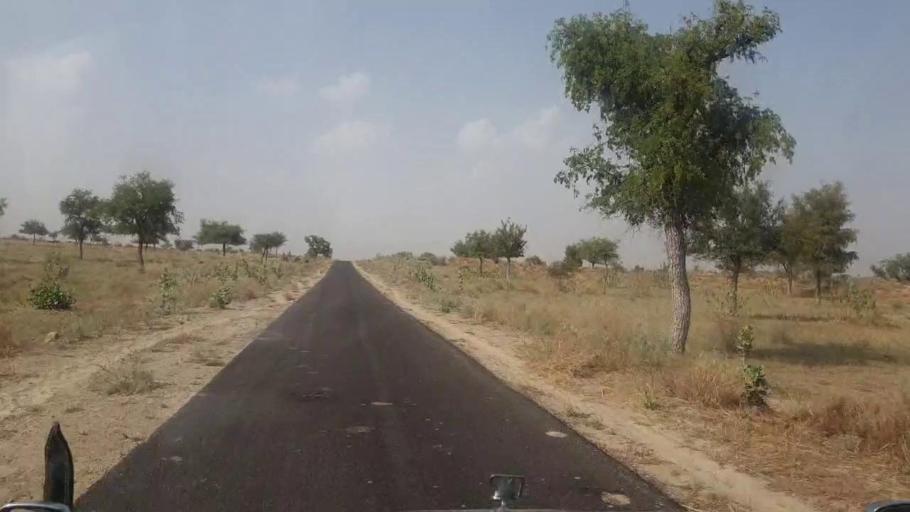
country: PK
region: Sindh
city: Islamkot
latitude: 25.1777
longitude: 70.2878
